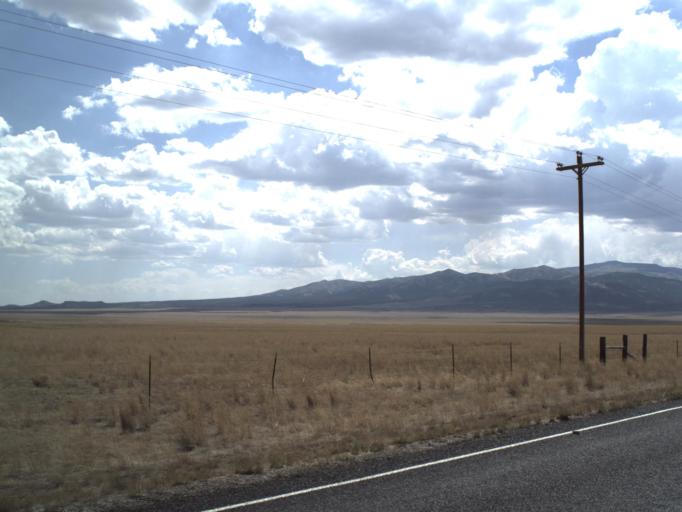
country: US
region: Idaho
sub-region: Oneida County
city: Malad City
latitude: 41.9654
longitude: -113.0584
